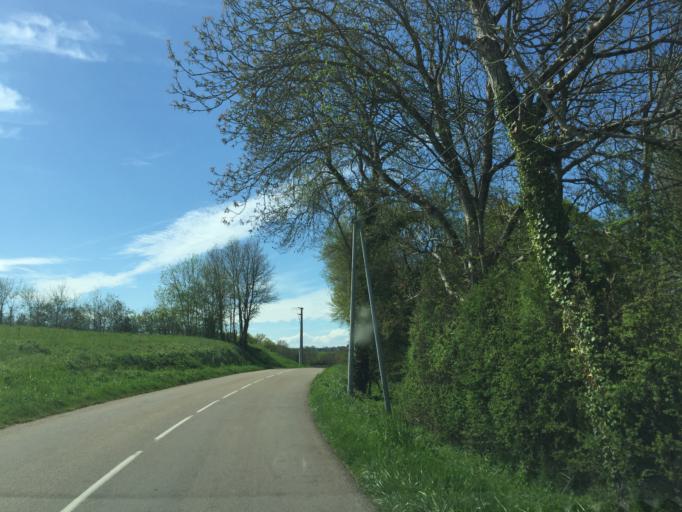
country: FR
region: Rhone-Alpes
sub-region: Departement de l'Isere
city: Trept
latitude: 45.7107
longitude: 5.3454
